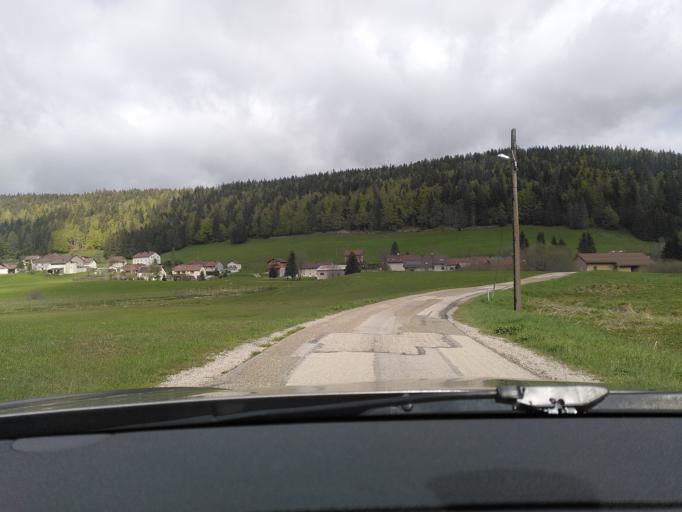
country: FR
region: Franche-Comte
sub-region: Departement du Jura
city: Les Rousses
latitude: 46.5304
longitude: 6.1308
